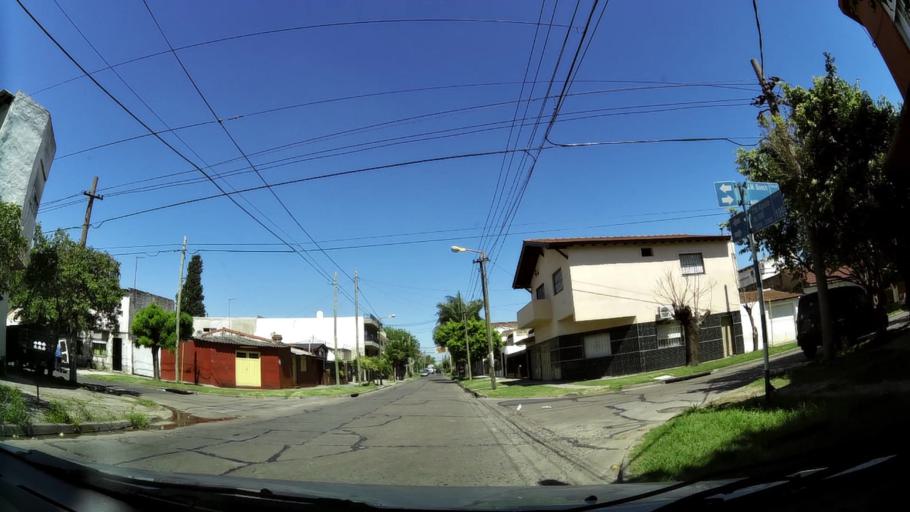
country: AR
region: Buenos Aires
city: Caseros
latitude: -34.5734
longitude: -58.5564
